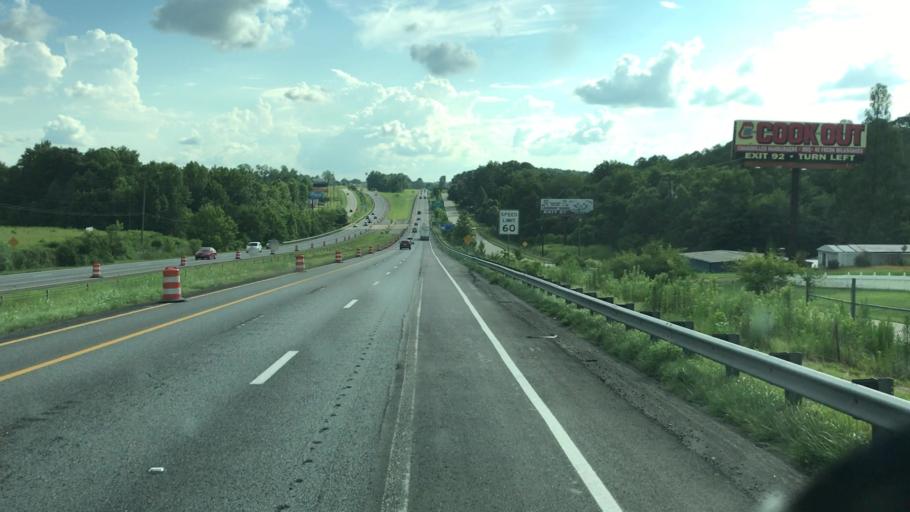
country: US
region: South Carolina
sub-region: Cherokee County
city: East Gaffney
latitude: 35.1081
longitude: -81.6090
